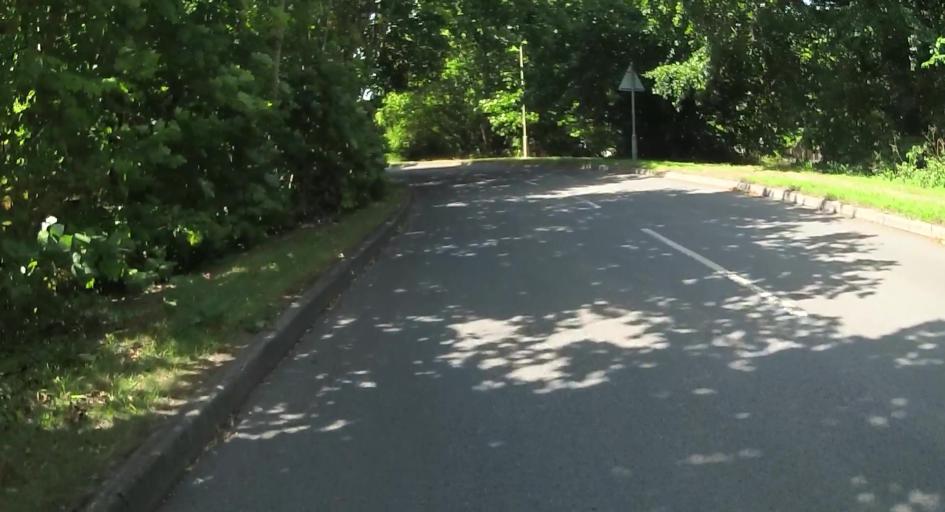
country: GB
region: England
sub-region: Hampshire
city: Old Basing
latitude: 51.2777
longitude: -1.0582
